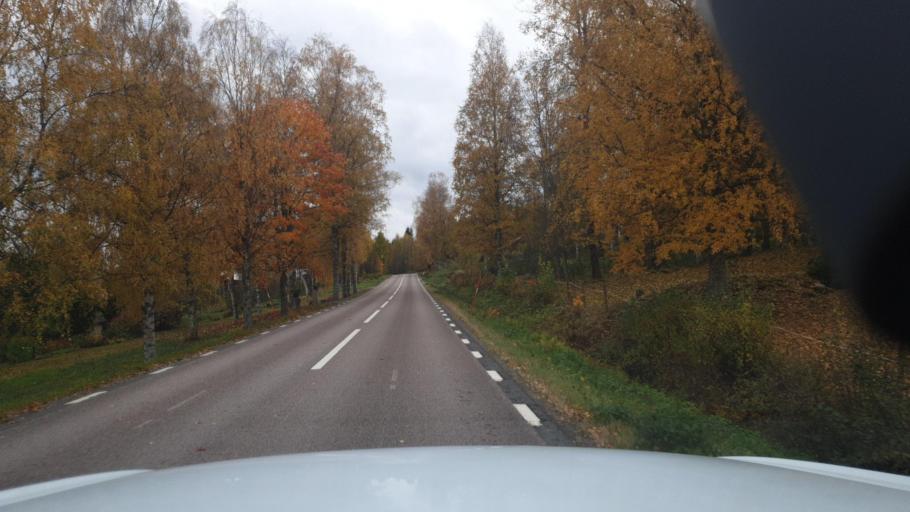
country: SE
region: Vaermland
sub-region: Torsby Kommun
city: Torsby
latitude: 59.9203
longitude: 12.8977
